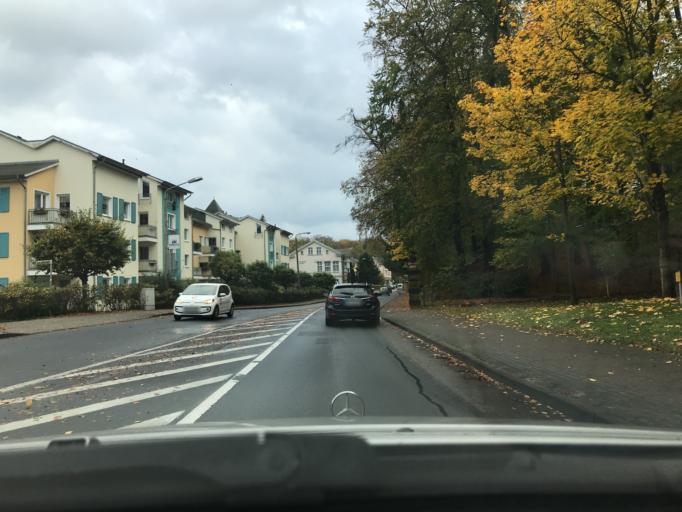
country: DE
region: Mecklenburg-Vorpommern
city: Seebad Heringsdorf
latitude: 53.9531
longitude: 14.1643
